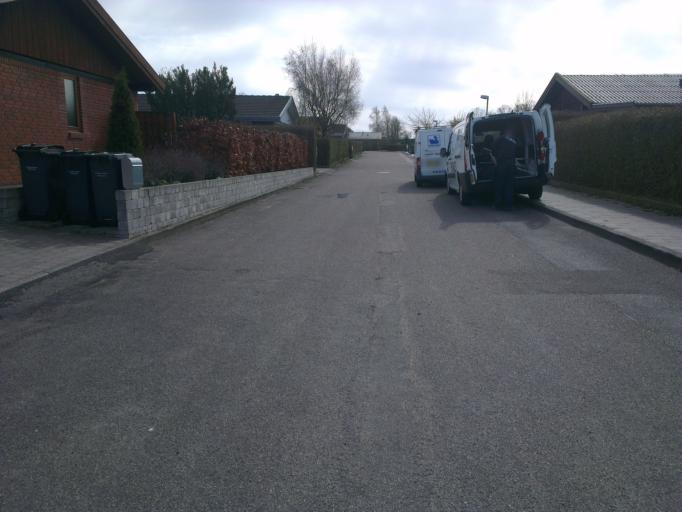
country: DK
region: Capital Region
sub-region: Frederikssund Kommune
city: Frederikssund
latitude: 55.8248
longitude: 12.0690
